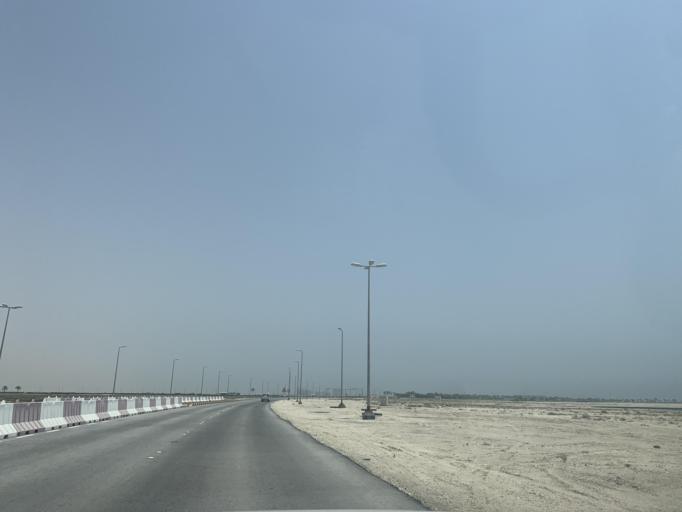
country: BH
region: Central Governorate
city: Dar Kulayb
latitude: 25.8422
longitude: 50.5935
